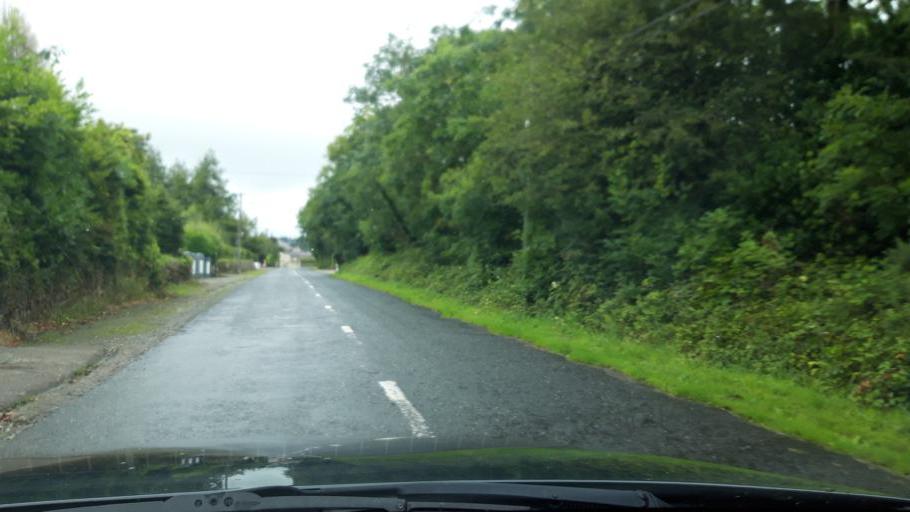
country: IE
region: Munster
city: Cahir
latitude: 52.1812
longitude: -7.8488
